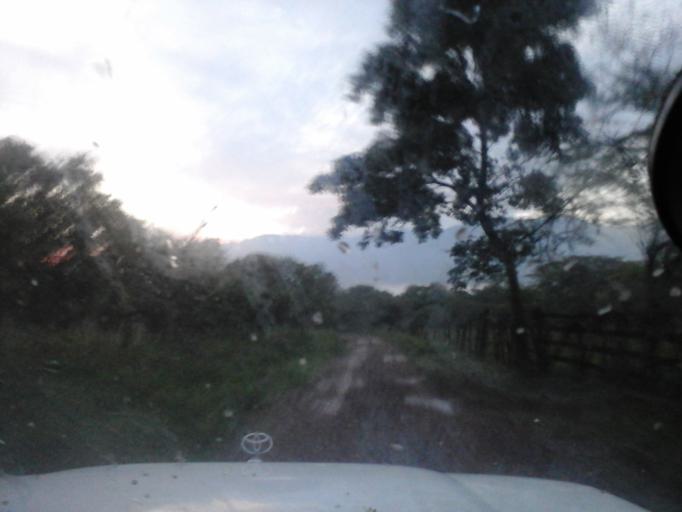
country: CO
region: Cesar
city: Agustin Codazzi
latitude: 10.1557
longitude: -73.2131
